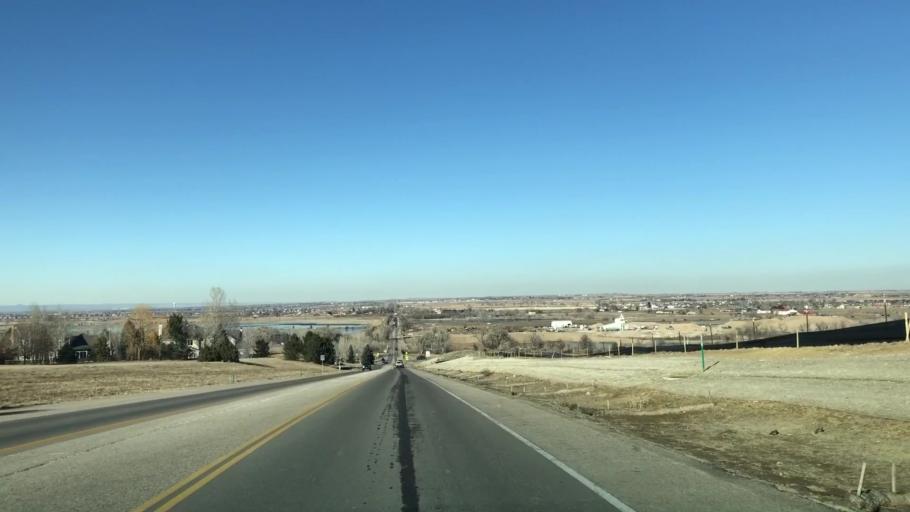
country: US
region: Colorado
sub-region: Weld County
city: Windsor
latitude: 40.4676
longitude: -104.9441
